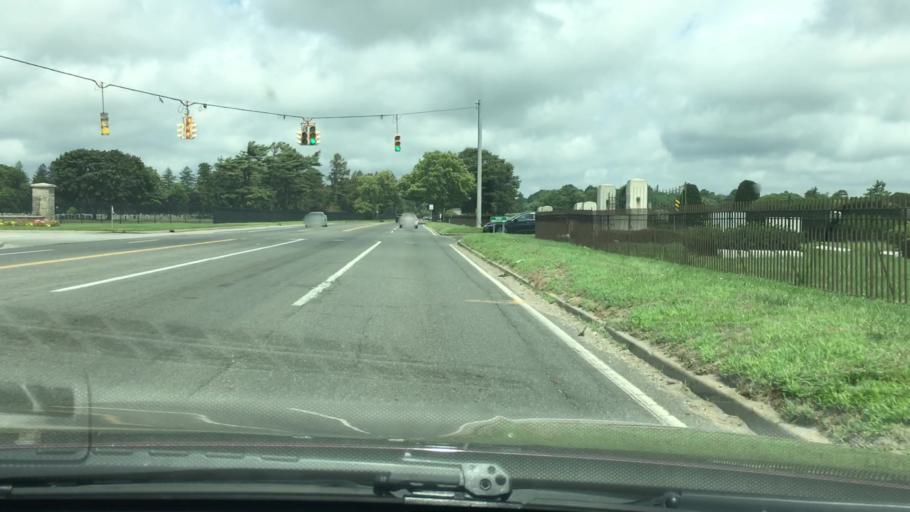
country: US
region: New York
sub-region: Suffolk County
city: East Farmingdale
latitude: 40.7347
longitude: -73.3988
